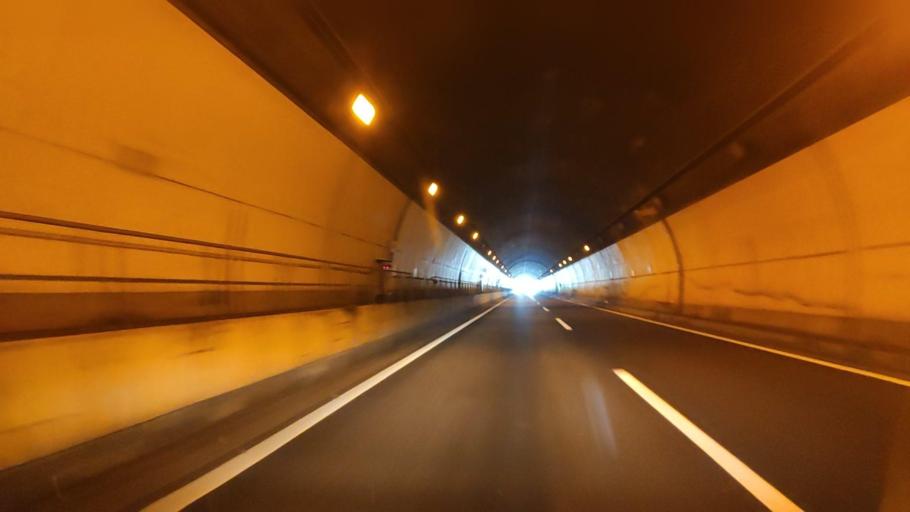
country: JP
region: Akita
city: Hanawa
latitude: 40.0165
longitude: 140.9858
